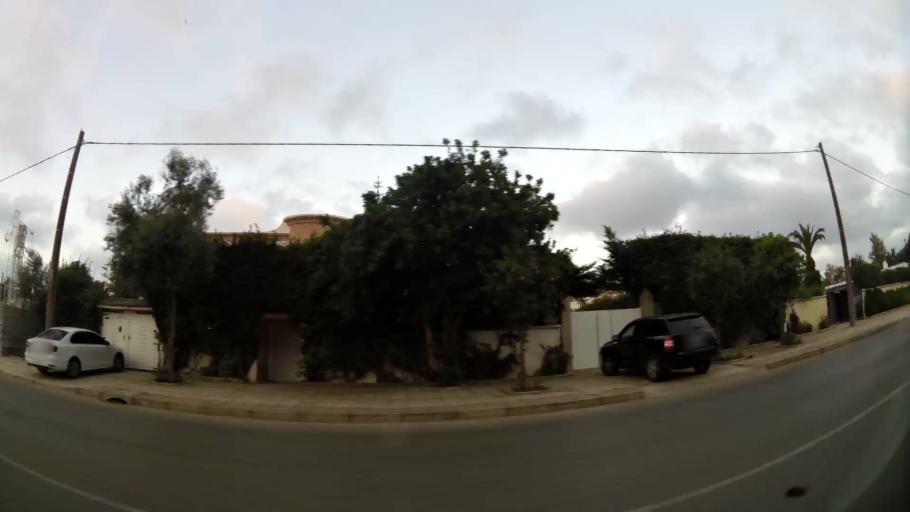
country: MA
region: Rabat-Sale-Zemmour-Zaer
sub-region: Rabat
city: Rabat
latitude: 33.9634
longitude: -6.8373
